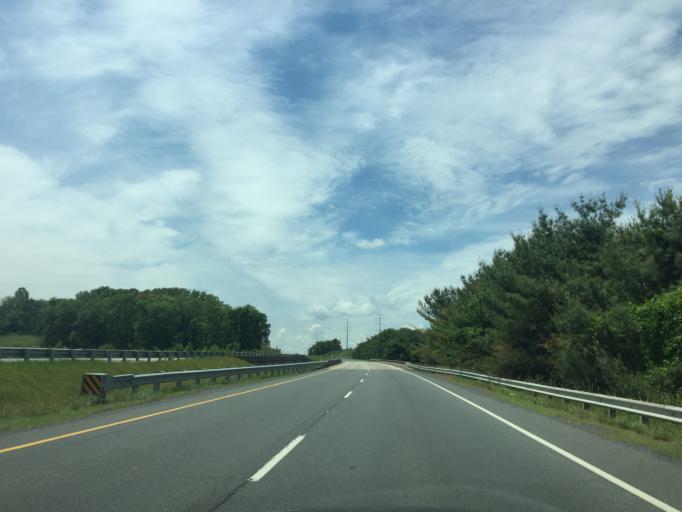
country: US
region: Virginia
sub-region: City of Winchester
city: Winchester
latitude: 39.2113
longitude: -78.1801
